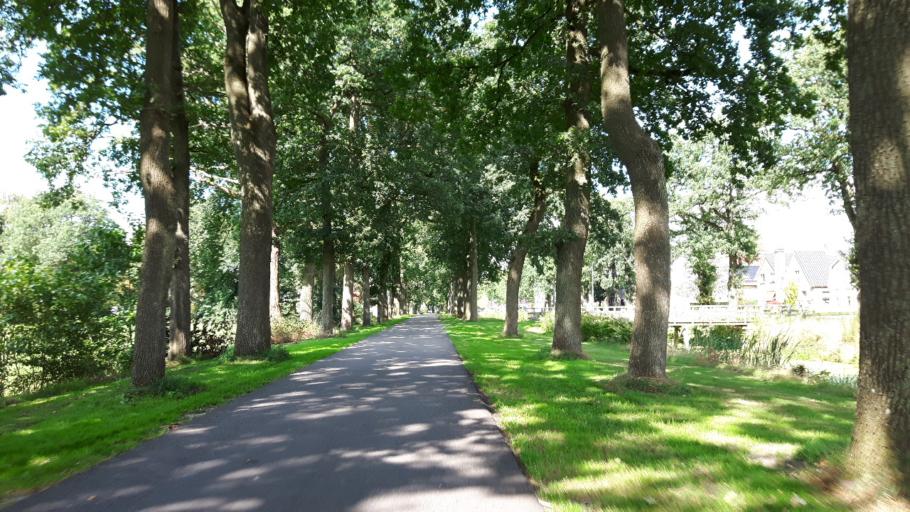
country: NL
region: Friesland
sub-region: Gemeente Smallingerland
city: Drachtstercompagnie
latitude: 53.0781
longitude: 6.2593
